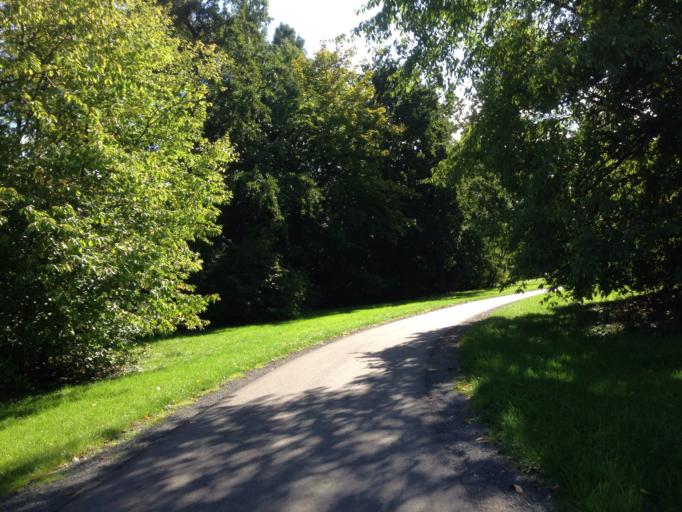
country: DE
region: Hesse
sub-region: Regierungsbezirk Giessen
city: Giessen
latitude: 50.5922
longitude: 8.6881
